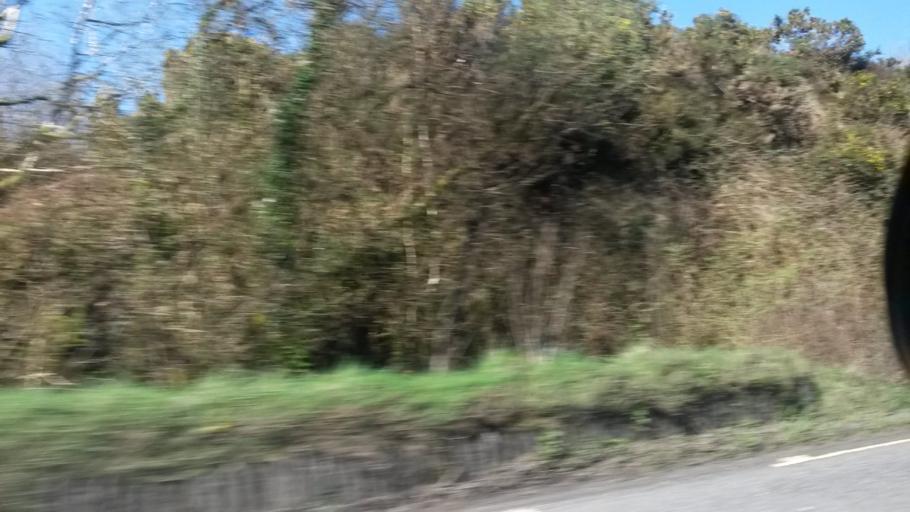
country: IE
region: Munster
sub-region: County Cork
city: Millstreet
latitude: 51.9254
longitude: -9.1183
